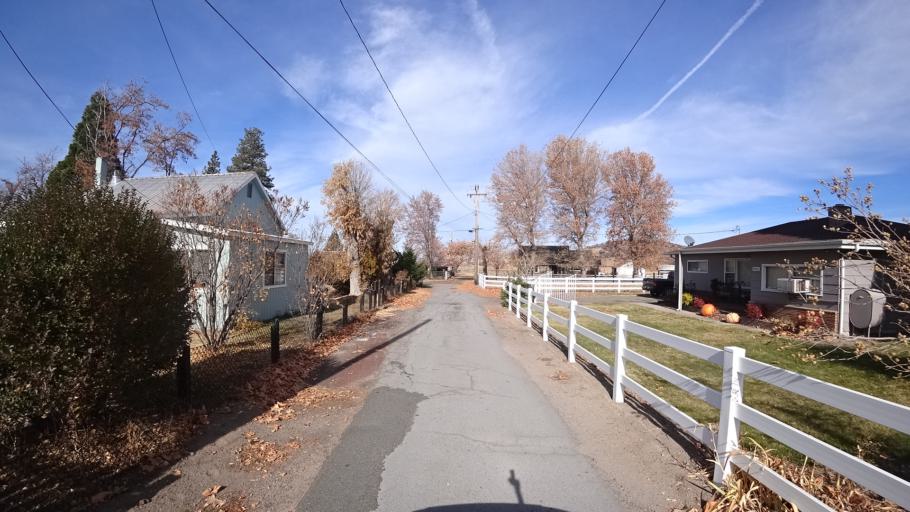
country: US
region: California
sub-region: Siskiyou County
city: Weed
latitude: 41.4595
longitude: -122.4310
